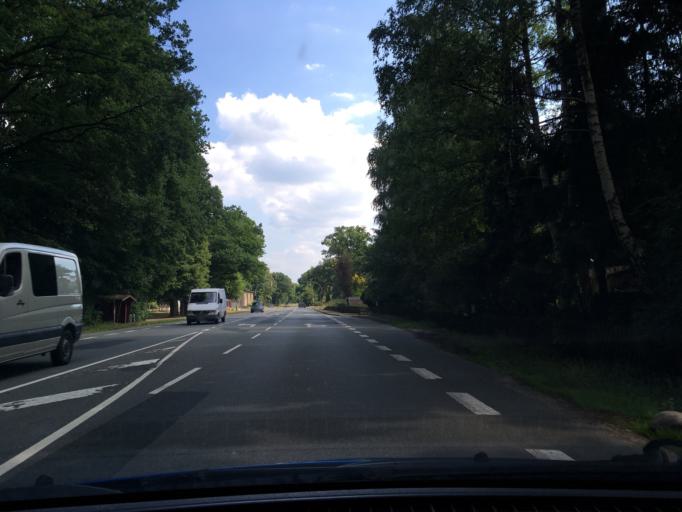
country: DE
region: Lower Saxony
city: Welle
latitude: 53.2552
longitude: 9.8068
